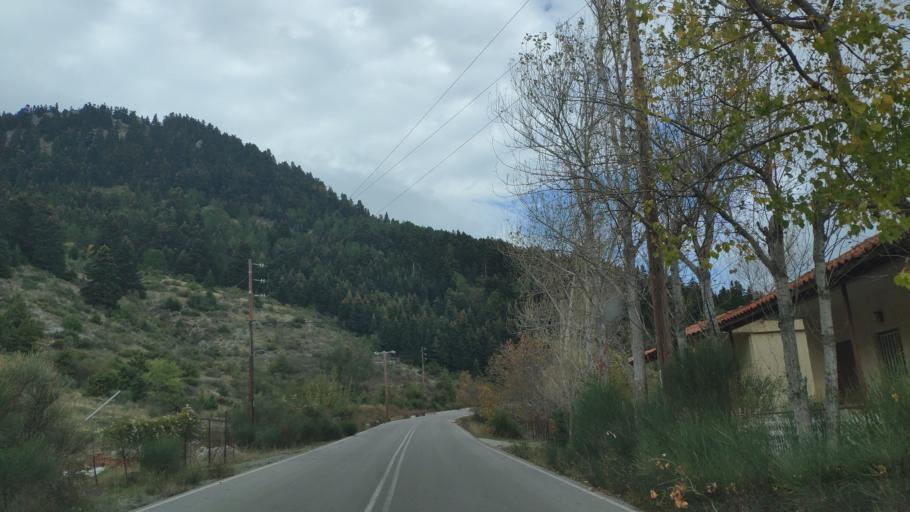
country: GR
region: Central Greece
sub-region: Nomos Fokidos
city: Amfissa
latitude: 38.6861
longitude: 22.3195
